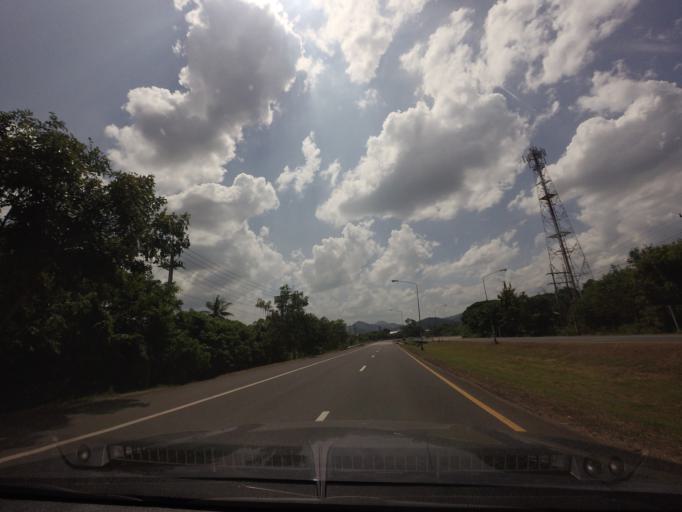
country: TH
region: Phetchabun
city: Phetchabun
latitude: 16.2691
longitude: 101.0564
